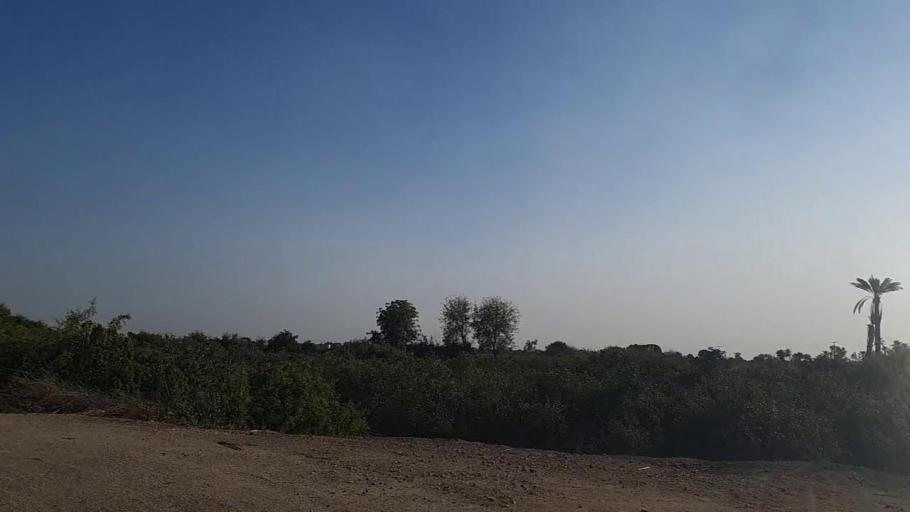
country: PK
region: Sindh
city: Shahpur Chakar
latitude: 26.2151
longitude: 68.6417
